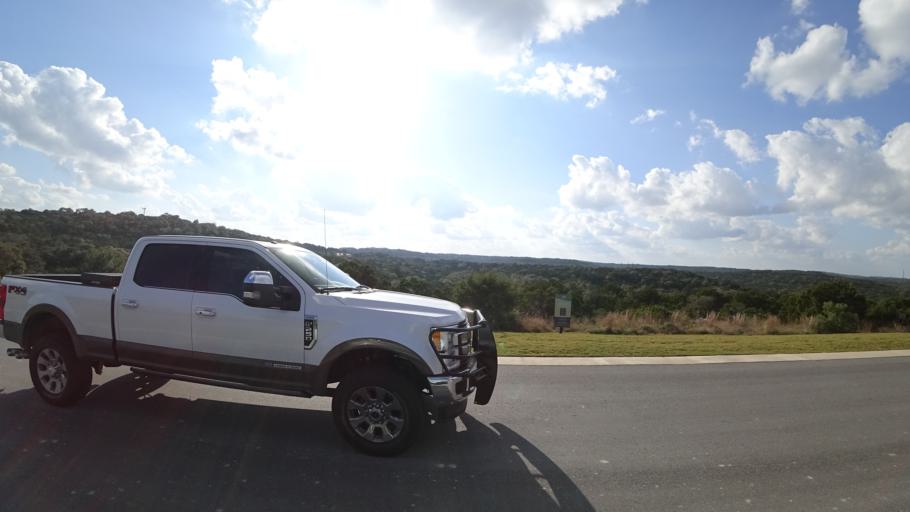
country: US
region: Texas
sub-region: Travis County
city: Barton Creek
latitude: 30.2659
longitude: -97.8836
